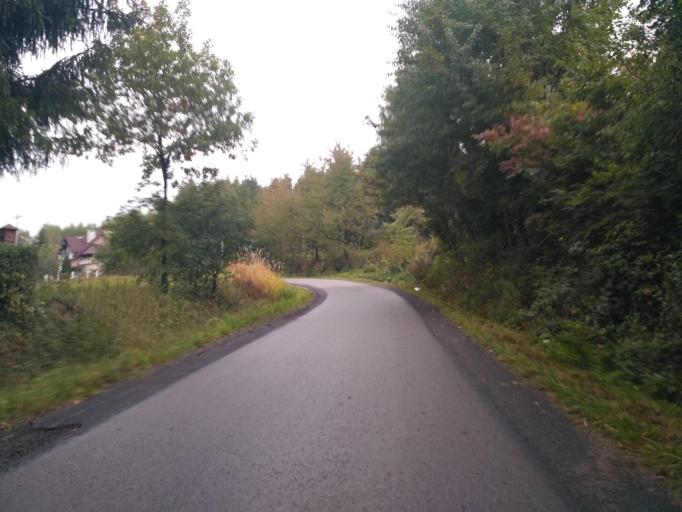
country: PL
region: Subcarpathian Voivodeship
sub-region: Powiat debicki
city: Brzostek
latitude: 49.9239
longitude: 21.4644
